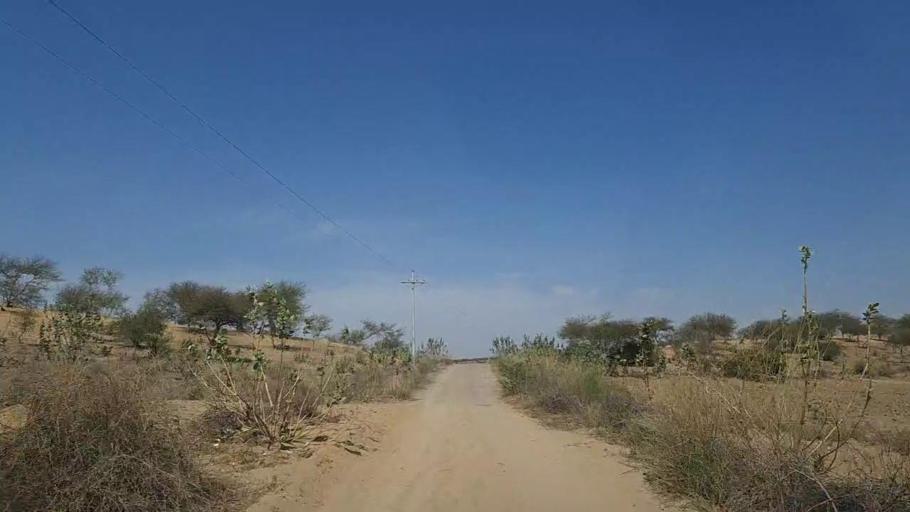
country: PK
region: Sindh
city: Mithi
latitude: 24.8421
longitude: 69.6675
